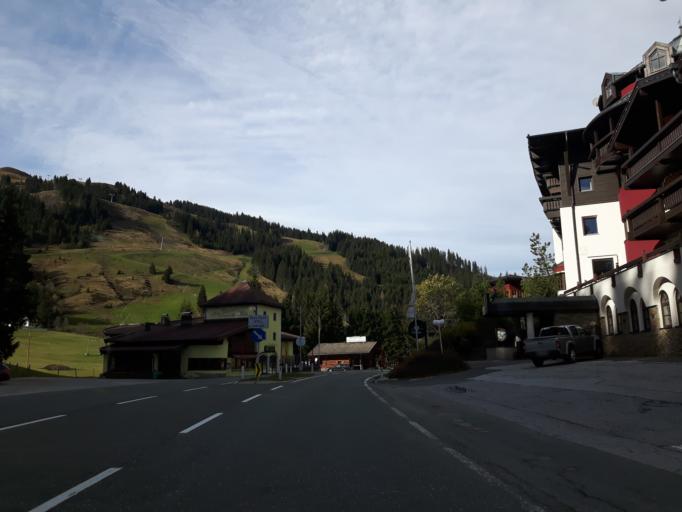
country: AT
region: Salzburg
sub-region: Politischer Bezirk Zell am See
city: Hollersbach im Pinzgau
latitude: 47.3106
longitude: 12.4087
